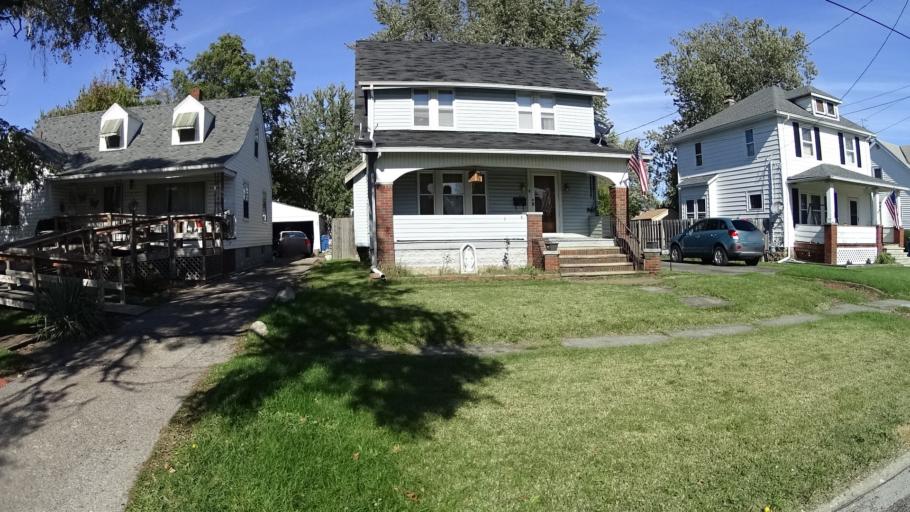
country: US
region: Ohio
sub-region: Lorain County
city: Lorain
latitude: 41.4529
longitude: -82.1771
